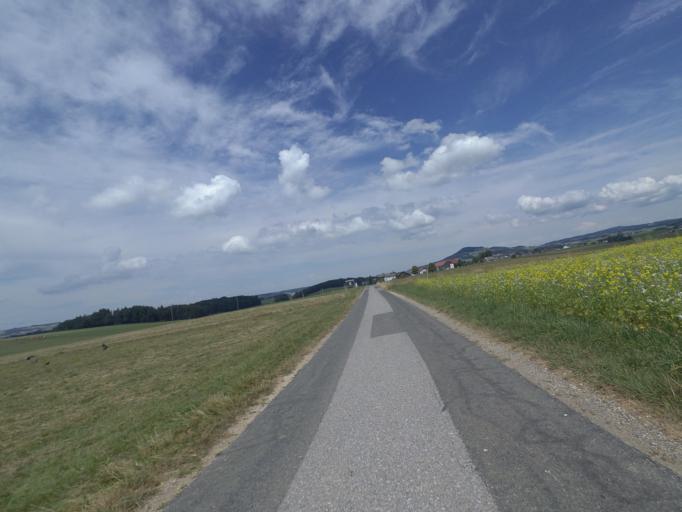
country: AT
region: Salzburg
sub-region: Politischer Bezirk Salzburg-Umgebung
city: Obertrum am See
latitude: 47.9081
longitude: 13.0923
